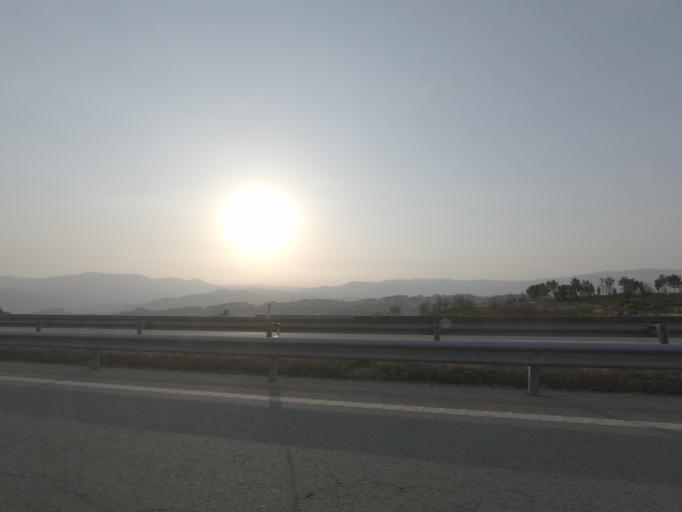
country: PT
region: Vila Real
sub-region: Vila Real
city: Vila Real
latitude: 41.2498
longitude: -7.7168
